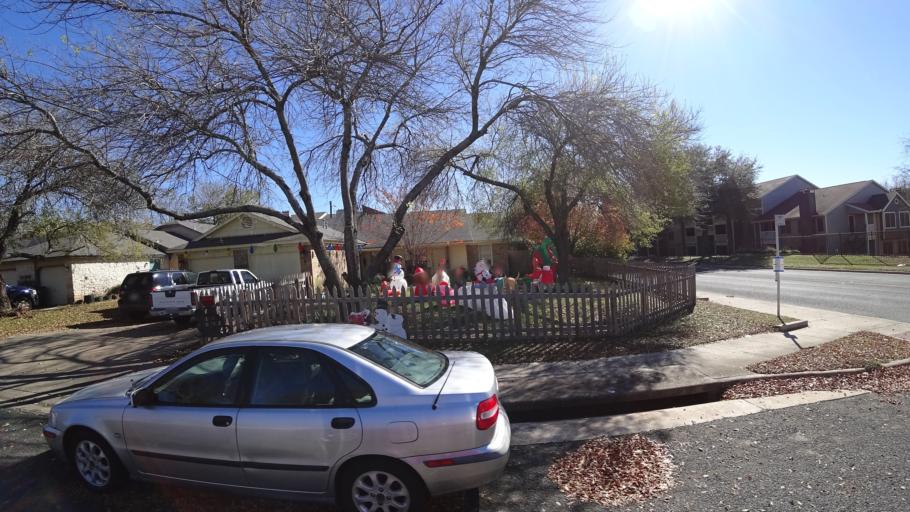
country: US
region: Texas
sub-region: Travis County
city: Wells Branch
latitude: 30.4103
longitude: -97.6998
